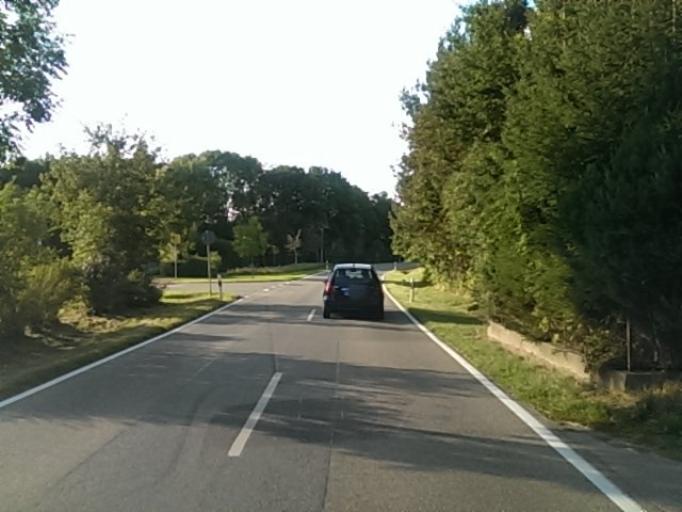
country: DE
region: Baden-Wuerttemberg
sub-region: Freiburg Region
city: Seedorf
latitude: 48.2968
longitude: 8.4897
